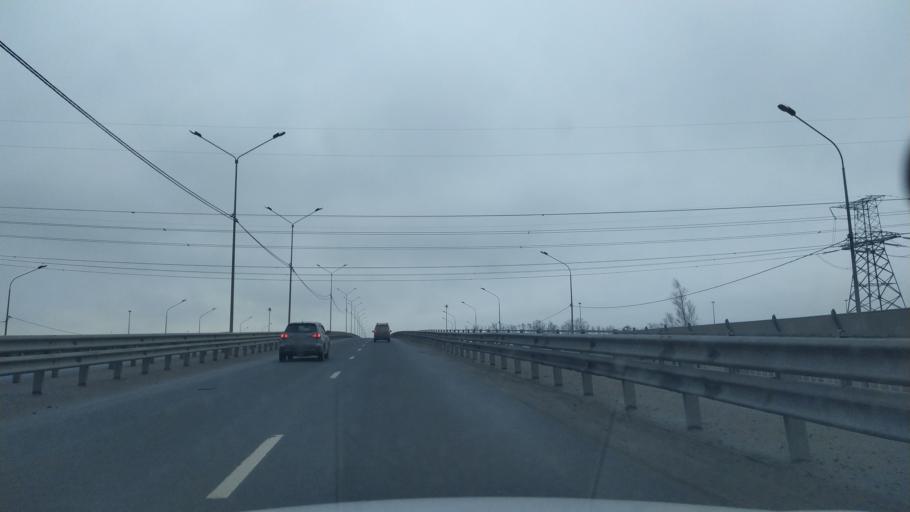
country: RU
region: St.-Petersburg
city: Aleksandrovskaya
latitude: 59.7190
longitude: 30.2784
